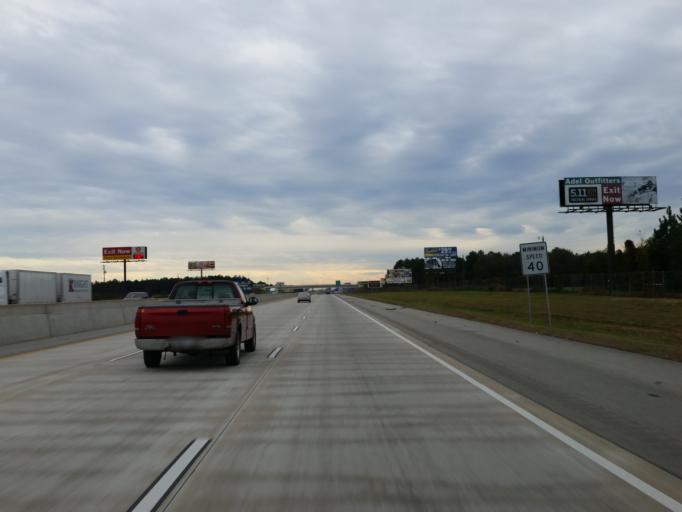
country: US
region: Georgia
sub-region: Cook County
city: Sparks
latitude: 31.1534
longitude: -83.4456
